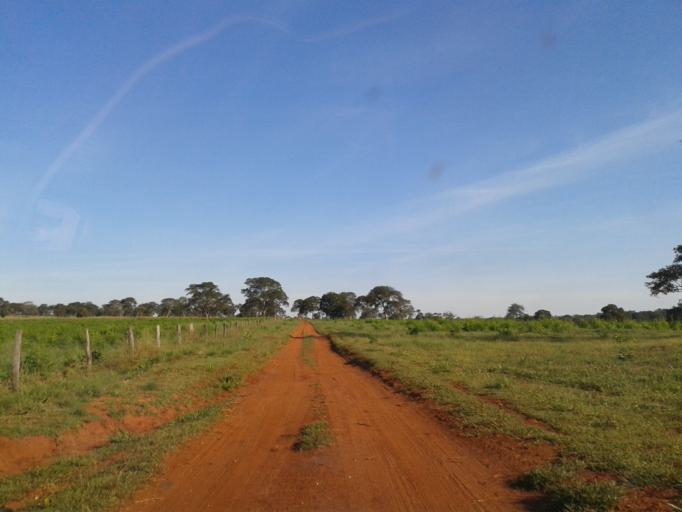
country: BR
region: Minas Gerais
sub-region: Santa Vitoria
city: Santa Vitoria
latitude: -19.0105
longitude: -50.3358
